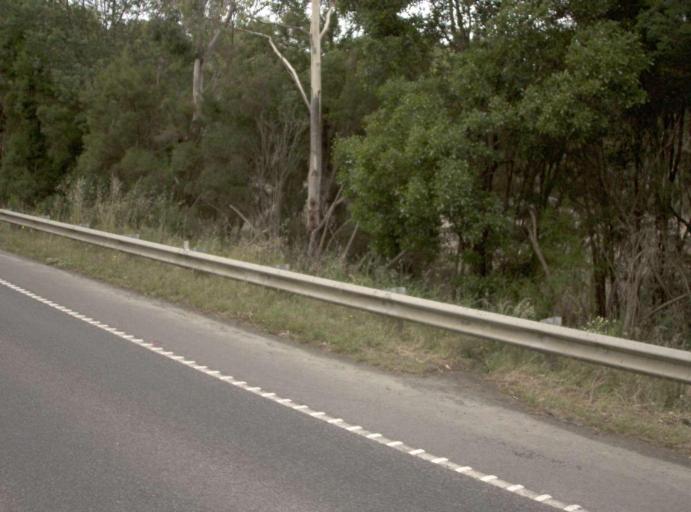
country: AU
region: Victoria
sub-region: Bass Coast
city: North Wonthaggi
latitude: -38.5426
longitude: 145.9475
